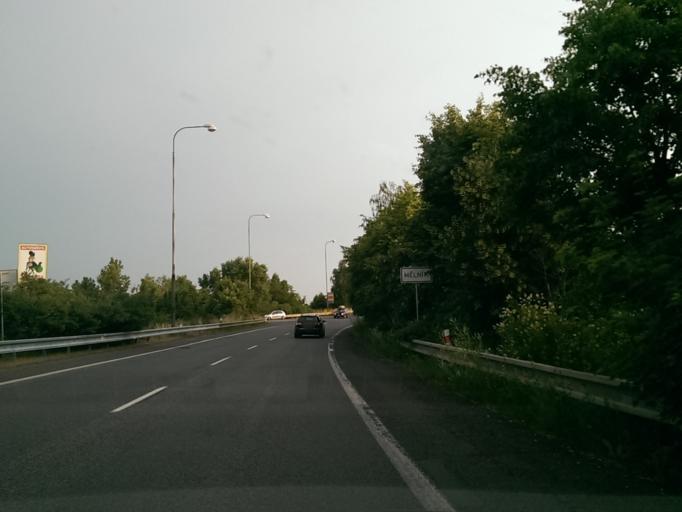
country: CZ
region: Central Bohemia
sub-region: Okres Melnik
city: Melnik
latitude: 50.3676
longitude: 14.4774
